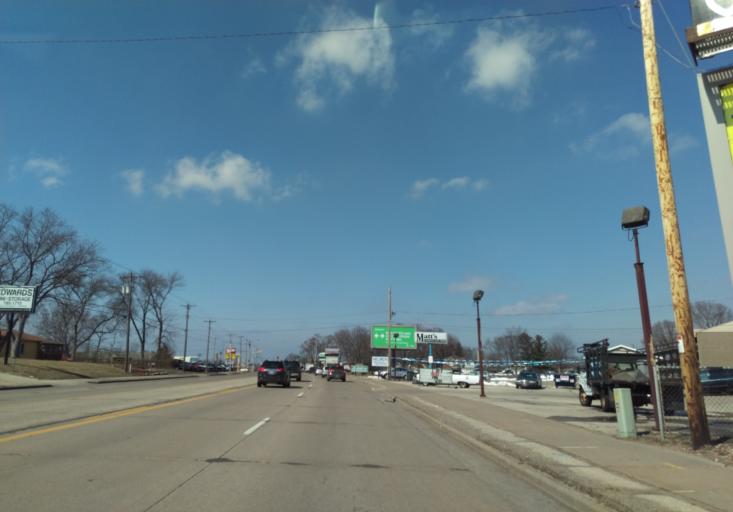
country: US
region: Wisconsin
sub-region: La Crosse County
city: La Crosse
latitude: 43.7680
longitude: -91.2123
